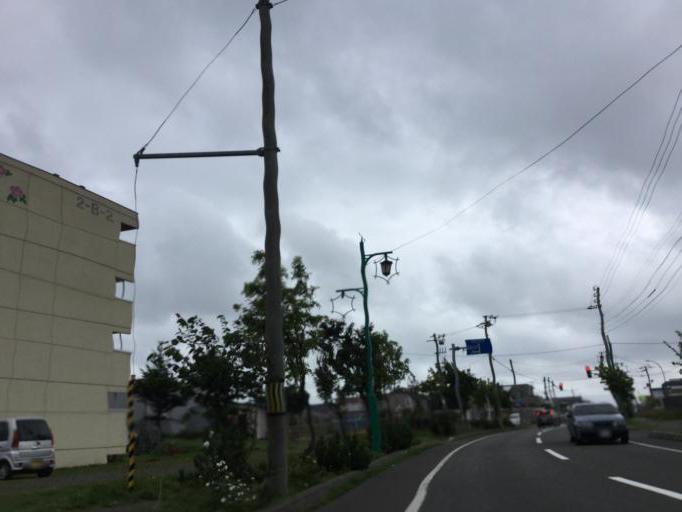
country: JP
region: Hokkaido
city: Wakkanai
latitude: 45.3932
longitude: 141.6996
